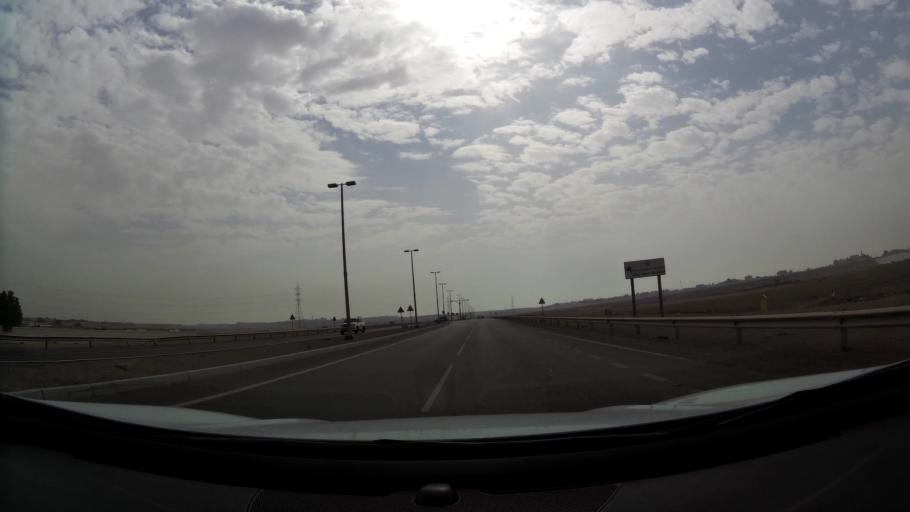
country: AE
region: Abu Dhabi
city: Abu Dhabi
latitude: 24.2855
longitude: 54.6669
